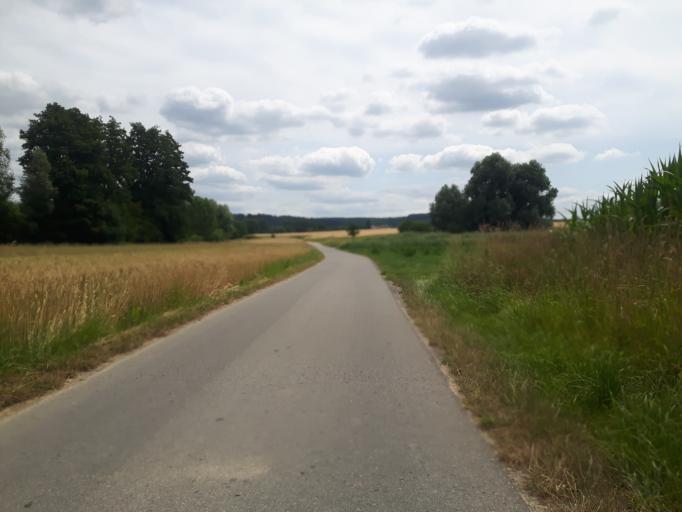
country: DE
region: Baden-Wuerttemberg
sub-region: Regierungsbezirk Stuttgart
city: Eppingen
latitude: 49.1136
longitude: 8.8910
